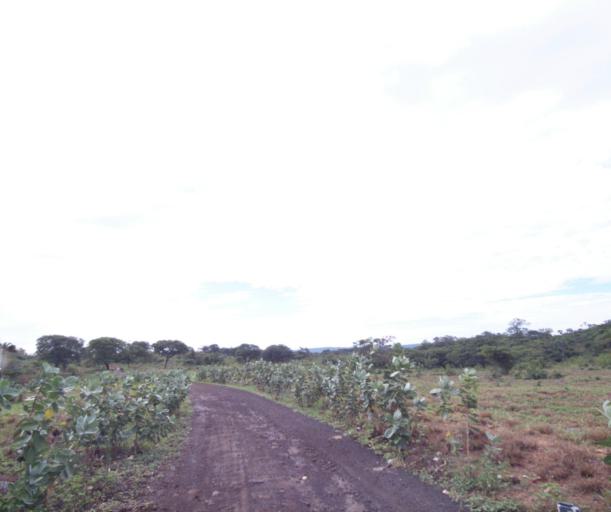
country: BR
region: Bahia
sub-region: Carinhanha
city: Carinhanha
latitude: -14.2271
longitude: -44.4345
